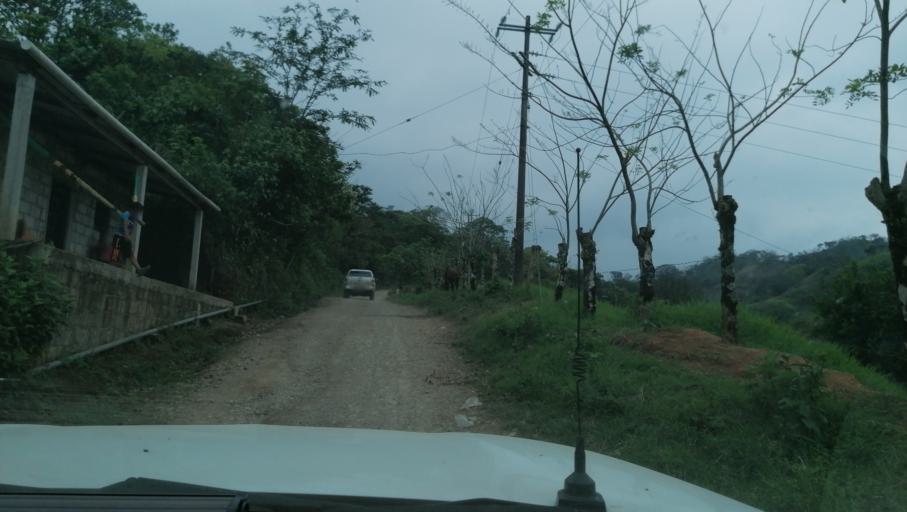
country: MX
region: Chiapas
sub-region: Francisco Leon
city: San Miguel la Sardina
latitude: 17.3273
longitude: -93.3109
